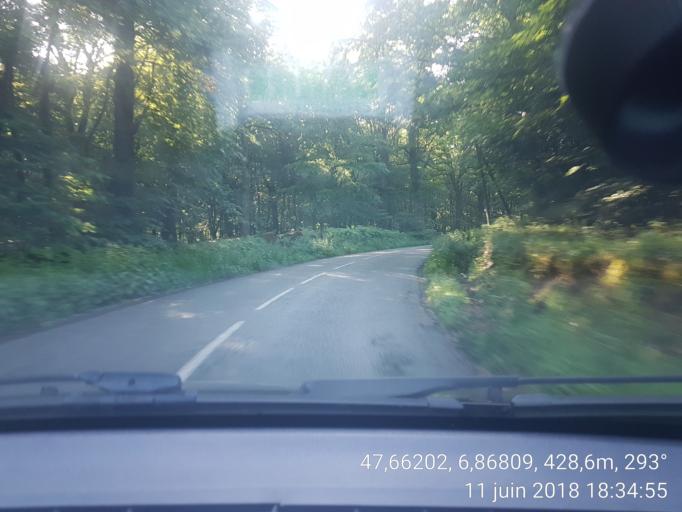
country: FR
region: Franche-Comte
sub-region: Territoire de Belfort
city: Offemont
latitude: 47.6619
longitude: 6.8683
